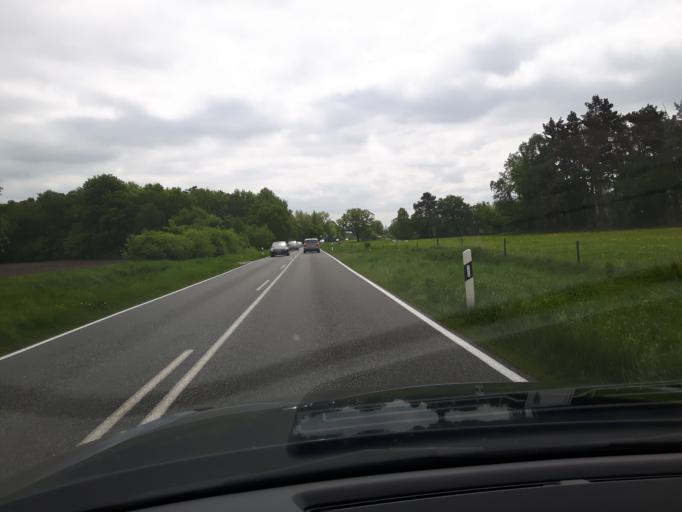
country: DE
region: Mecklenburg-Vorpommern
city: Ostseebad Dierhagen
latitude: 54.2557
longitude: 12.3565
